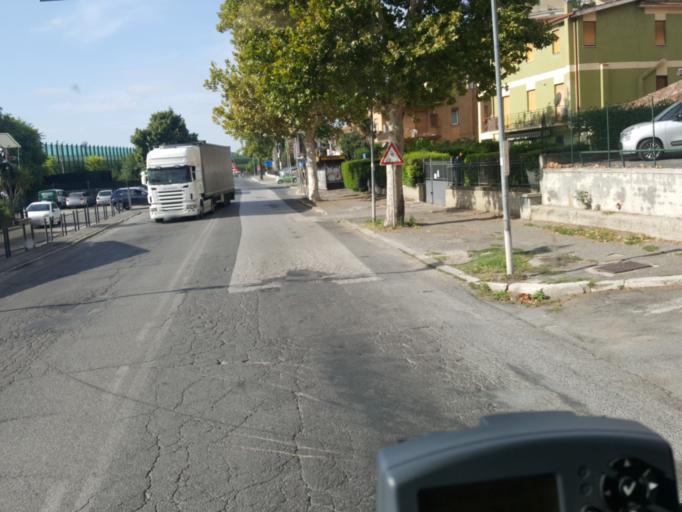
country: IT
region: Latium
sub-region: Citta metropolitana di Roma Capitale
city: Girardi-Bellavista-Terrazze
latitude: 42.1020
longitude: 12.5825
